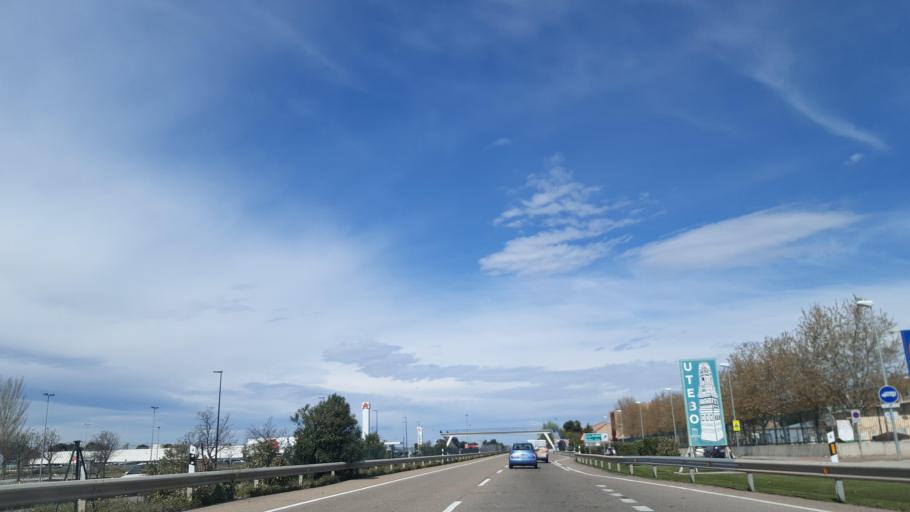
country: ES
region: Aragon
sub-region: Provincia de Zaragoza
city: Utebo
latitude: 41.7008
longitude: -0.9978
